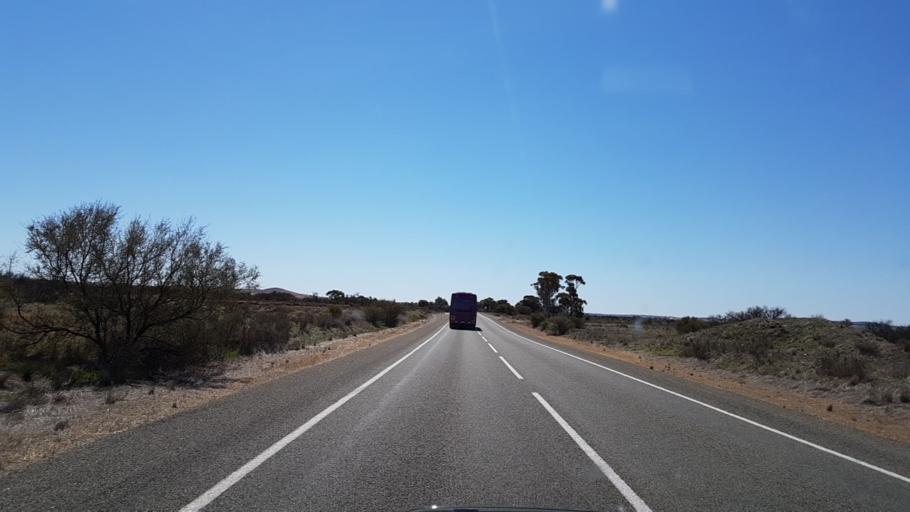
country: AU
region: South Australia
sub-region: Peterborough
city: Peterborough
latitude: -33.1847
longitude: 138.9051
